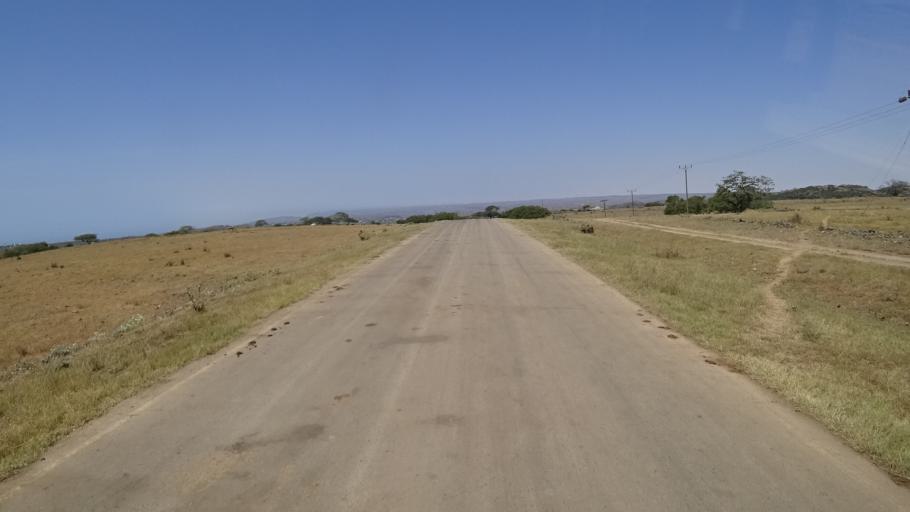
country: OM
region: Zufar
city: Salalah
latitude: 17.1216
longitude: 54.5884
